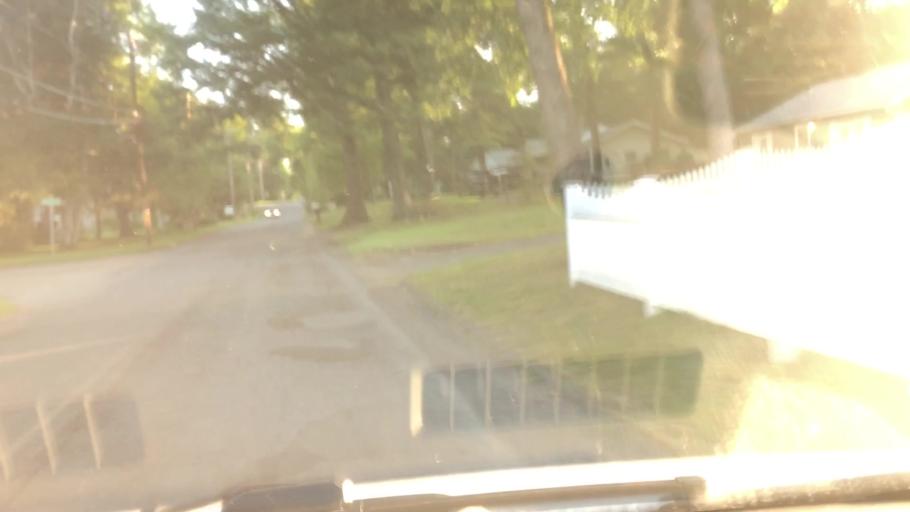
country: US
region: Massachusetts
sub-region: Hampshire County
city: Easthampton
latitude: 42.2963
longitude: -72.7168
